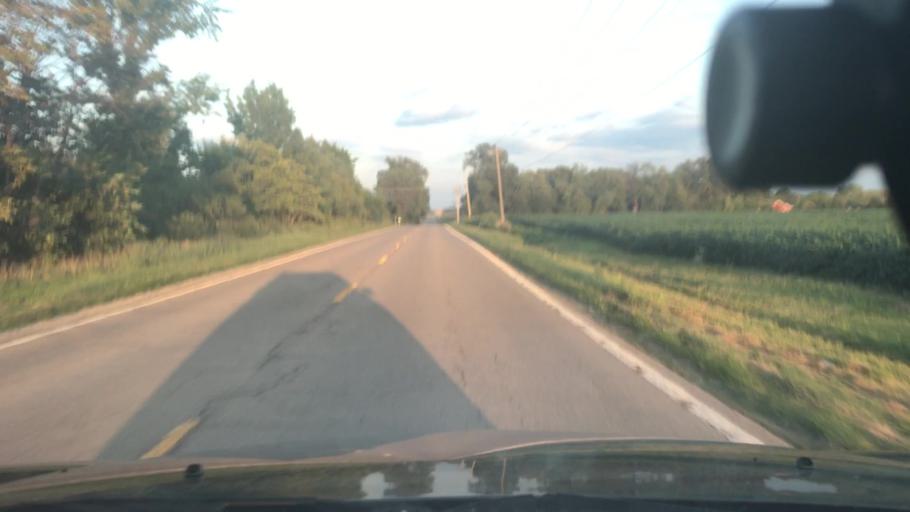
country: US
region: Illinois
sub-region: Washington County
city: Okawville
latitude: 38.4168
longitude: -89.5393
